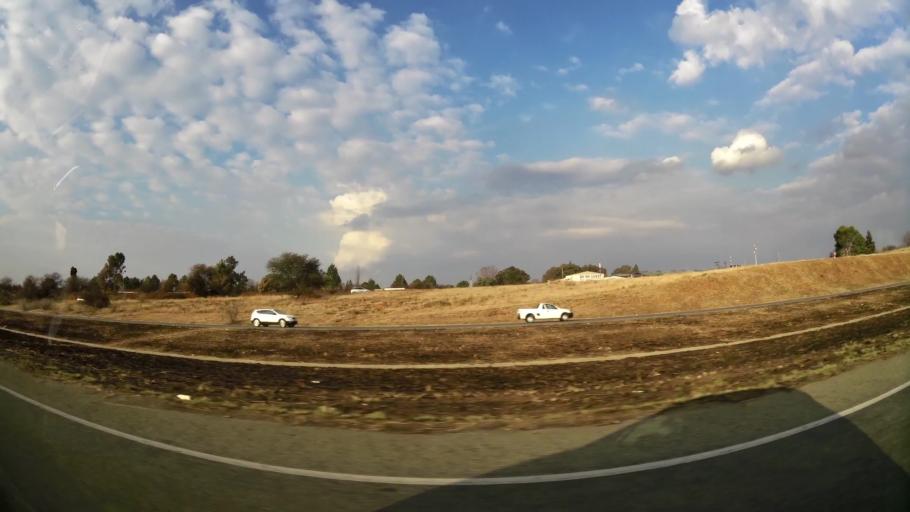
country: ZA
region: Gauteng
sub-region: Sedibeng District Municipality
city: Vanderbijlpark
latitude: -26.7593
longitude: 27.8248
